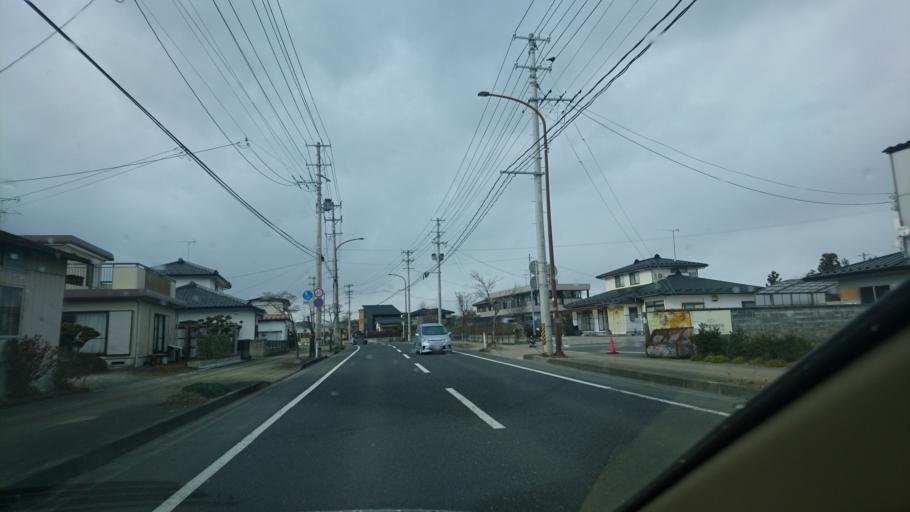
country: JP
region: Miyagi
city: Tomiya
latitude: 38.4419
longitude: 140.9019
